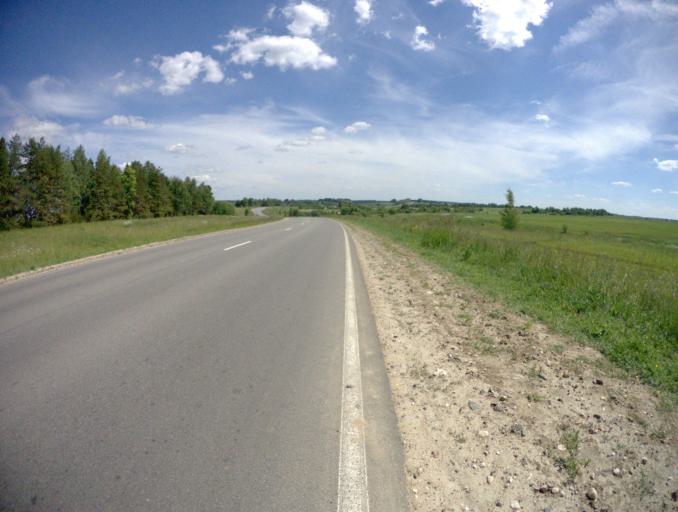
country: RU
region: Ivanovo
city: Gavrilov Posad
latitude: 56.3613
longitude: 40.0767
